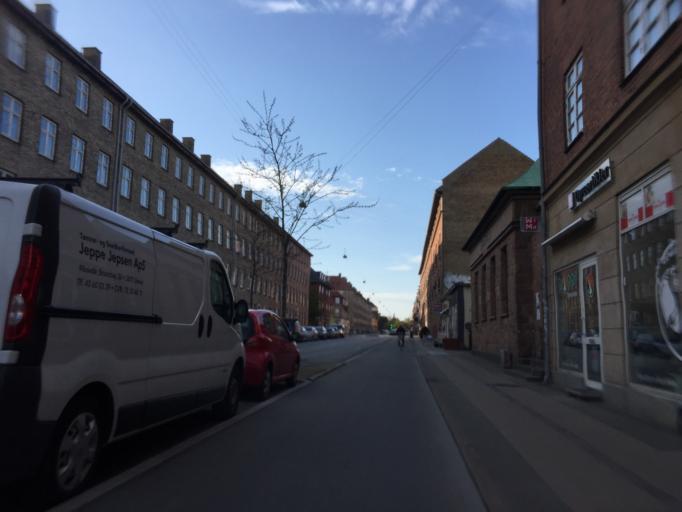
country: DK
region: Capital Region
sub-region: Kobenhavn
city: Vanlose
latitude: 55.6894
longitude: 12.4888
